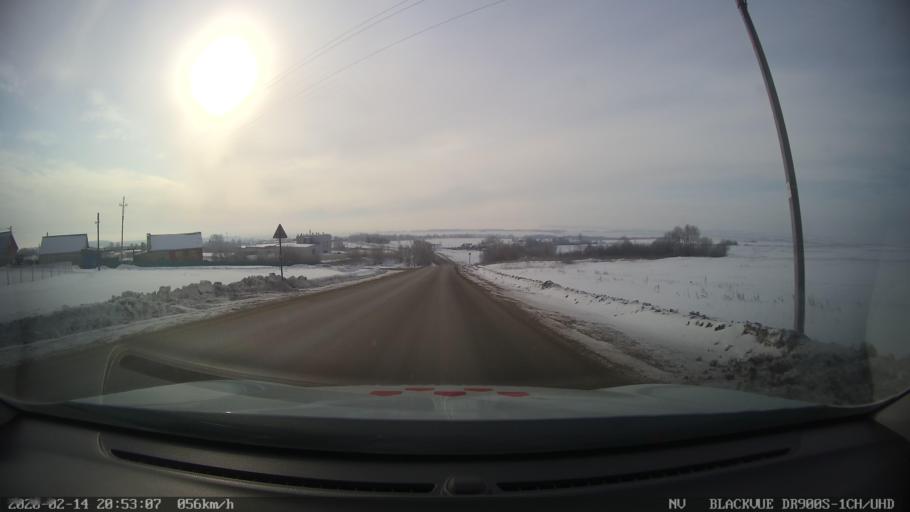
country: RU
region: Tatarstan
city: Kuybyshevskiy Zaton
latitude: 55.1977
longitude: 49.2483
